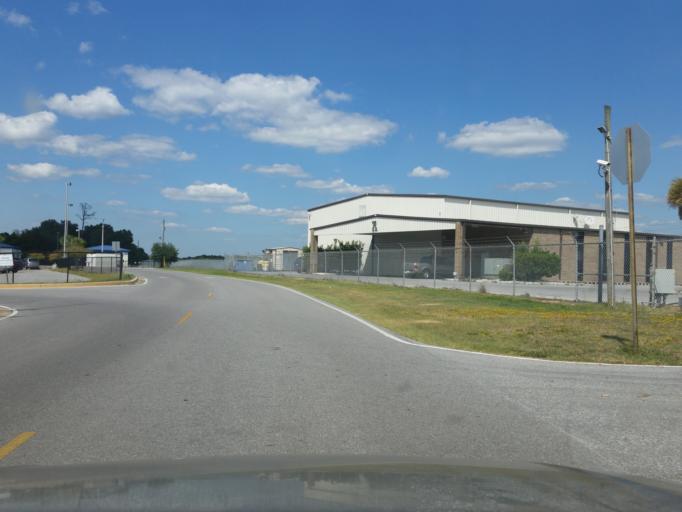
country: US
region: Florida
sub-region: Escambia County
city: Ferry Pass
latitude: 30.4795
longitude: -87.1929
